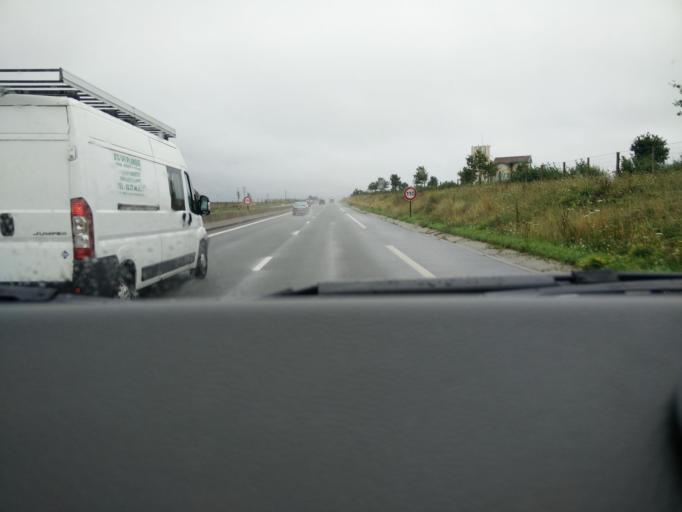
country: FR
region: Nord-Pas-de-Calais
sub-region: Departement du Pas-de-Calais
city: Marconnelle
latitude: 50.3680
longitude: 1.9562
